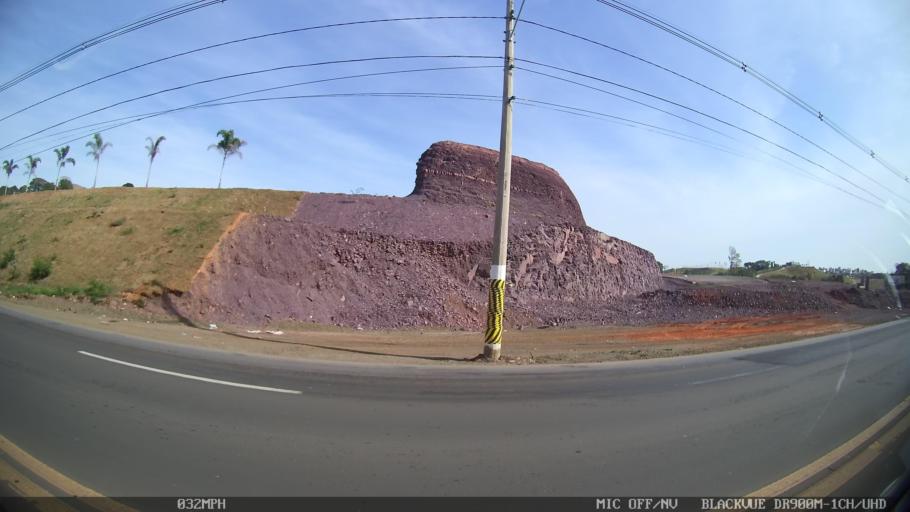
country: BR
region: Sao Paulo
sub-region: Piracicaba
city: Piracicaba
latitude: -22.7106
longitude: -47.6772
